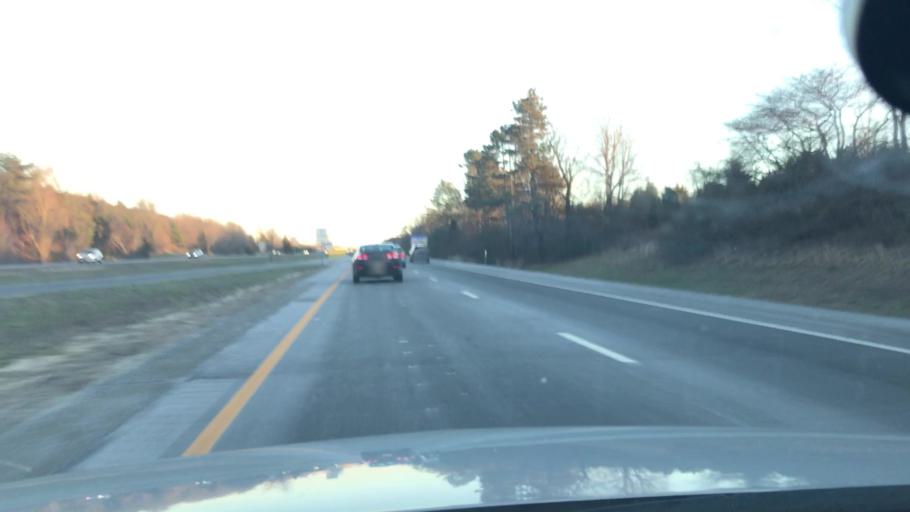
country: US
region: New Jersey
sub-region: Gloucester County
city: Turnersville
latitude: 39.7422
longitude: -75.0176
